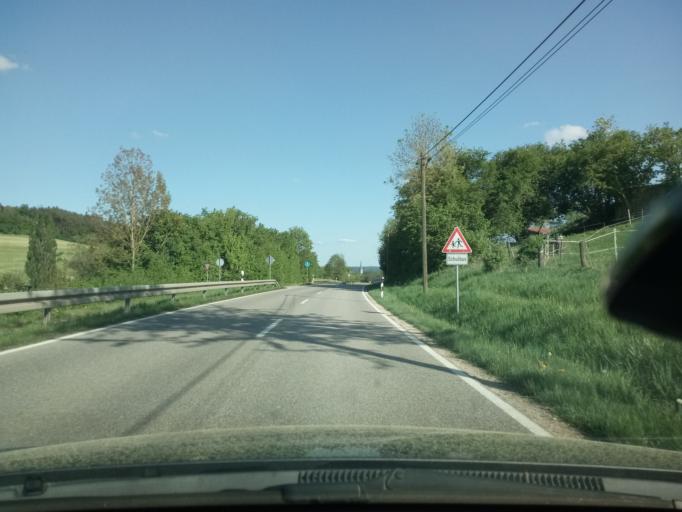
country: DE
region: Bavaria
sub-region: Upper Bavaria
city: Aschau am Inn
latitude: 48.2034
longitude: 12.3310
